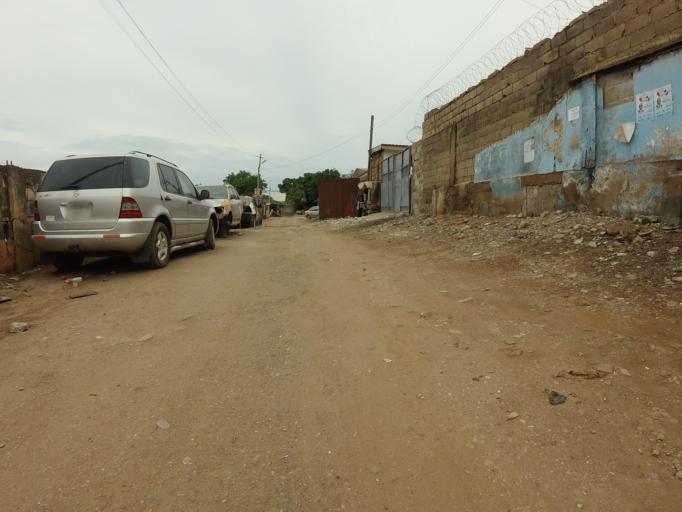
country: GH
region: Greater Accra
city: Accra
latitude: 5.5977
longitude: -0.2223
